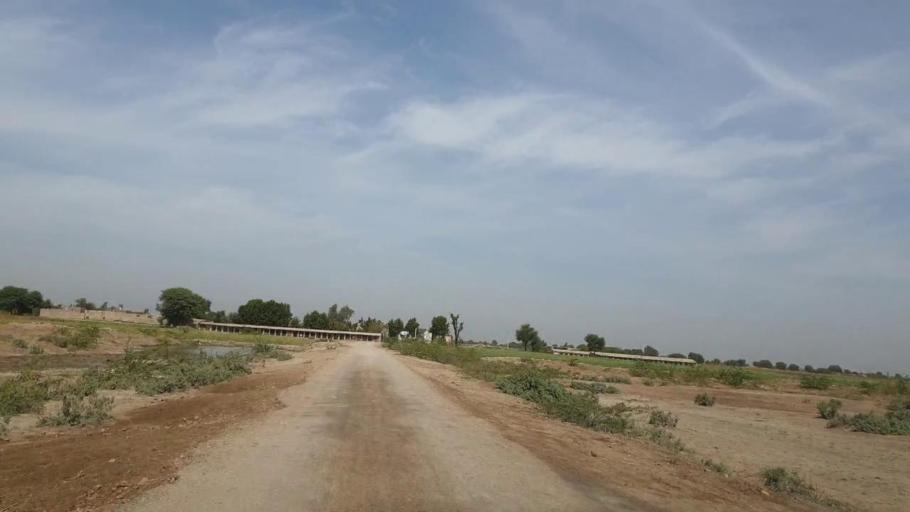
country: PK
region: Sindh
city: Kunri
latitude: 25.2171
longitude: 69.5739
